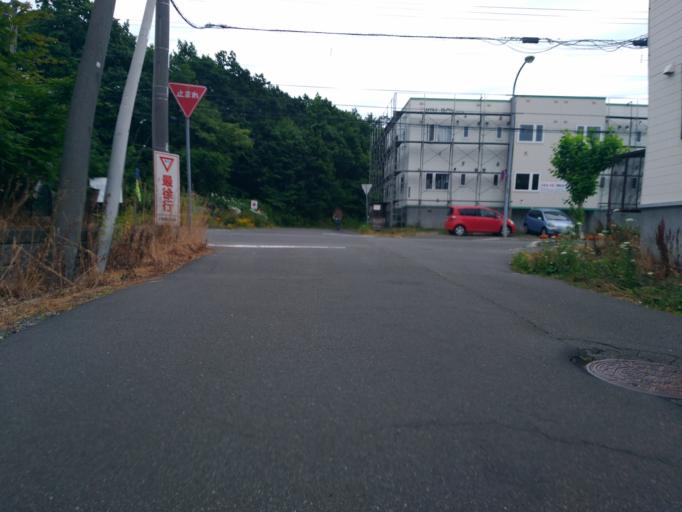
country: JP
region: Hokkaido
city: Ebetsu
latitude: 43.0655
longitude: 141.5022
